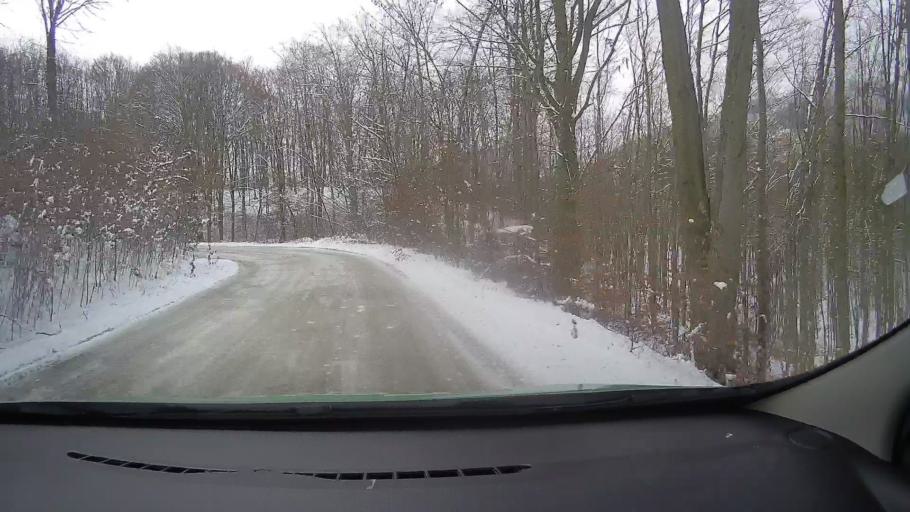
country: RO
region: Alba
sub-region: Comuna Almasu Mare
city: Almasu Mare
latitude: 46.0981
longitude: 23.1712
